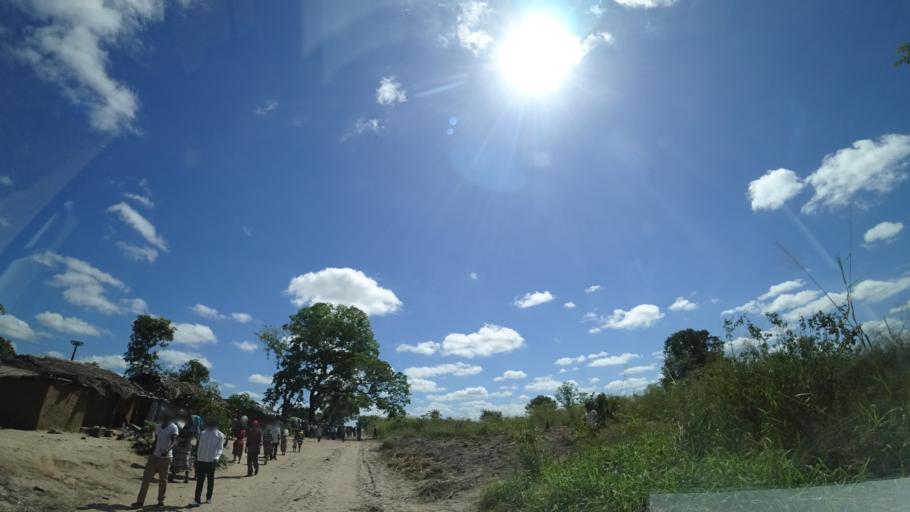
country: MZ
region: Sofala
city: Dondo
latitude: -19.2732
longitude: 34.6799
